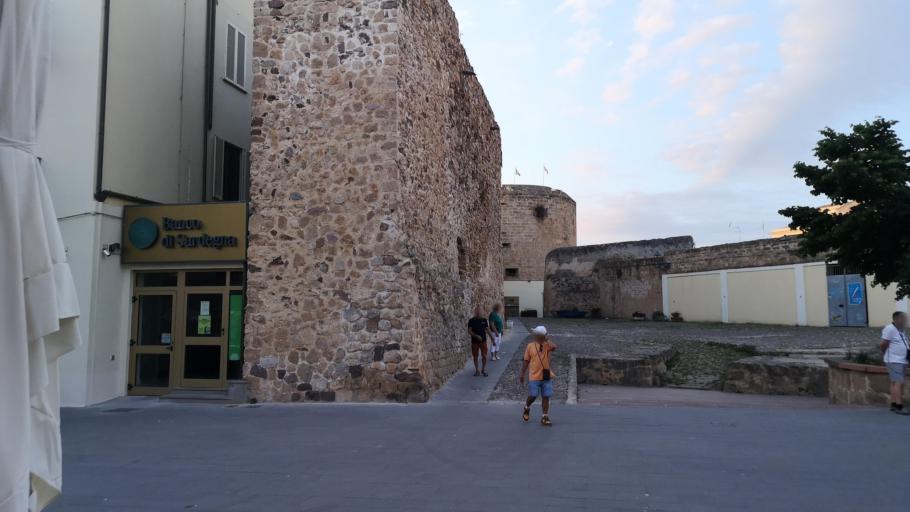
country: IT
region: Sardinia
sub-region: Provincia di Sassari
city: Alghero
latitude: 40.5576
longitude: 8.3155
